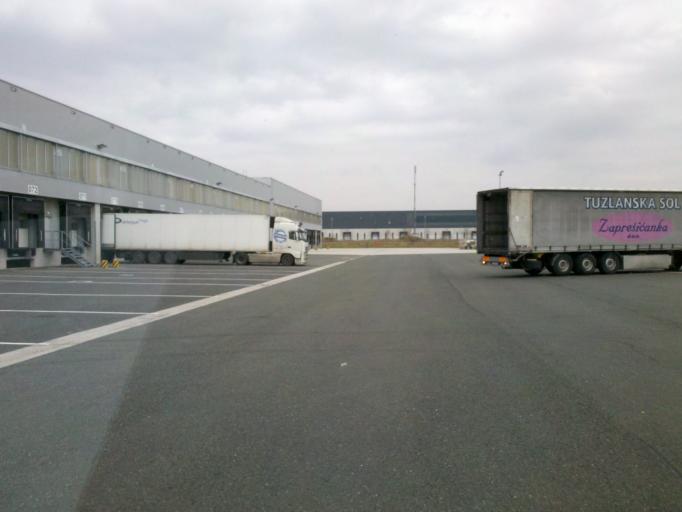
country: HR
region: Zagrebacka
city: Jastrebarsko
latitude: 45.6476
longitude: 15.6763
